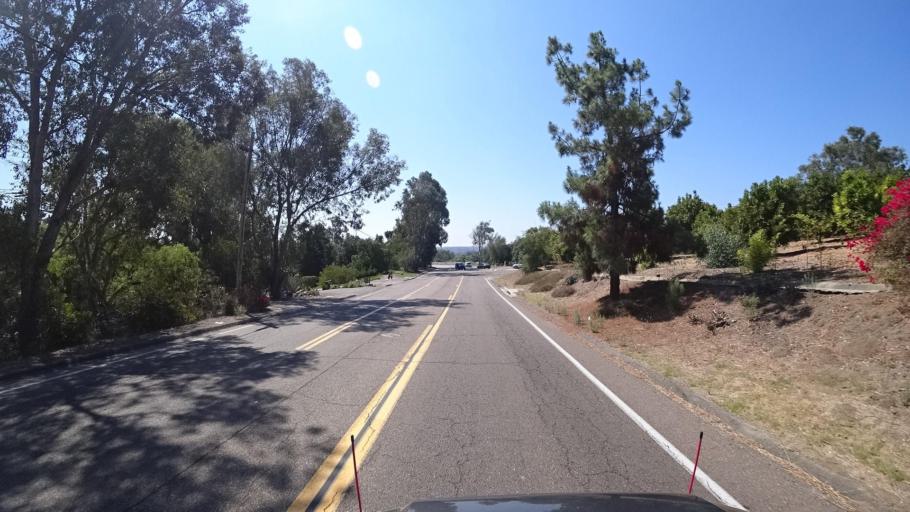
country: US
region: California
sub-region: San Diego County
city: Rancho Santa Fe
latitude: 33.0160
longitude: -117.1992
